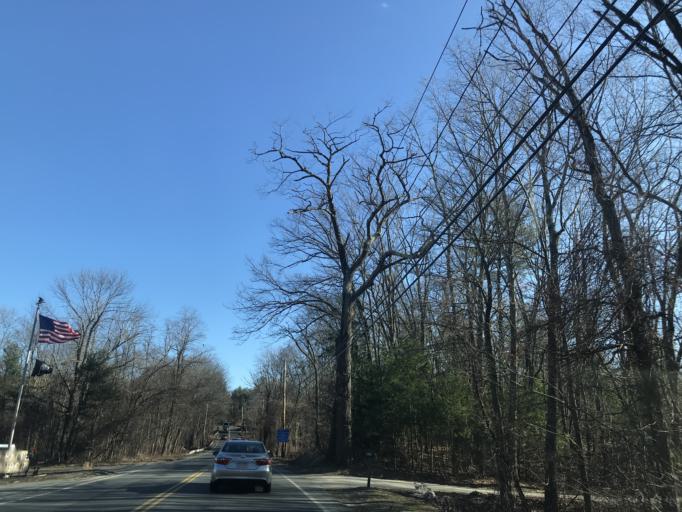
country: US
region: Massachusetts
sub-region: Essex County
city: Groveland
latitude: 42.7117
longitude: -71.0264
